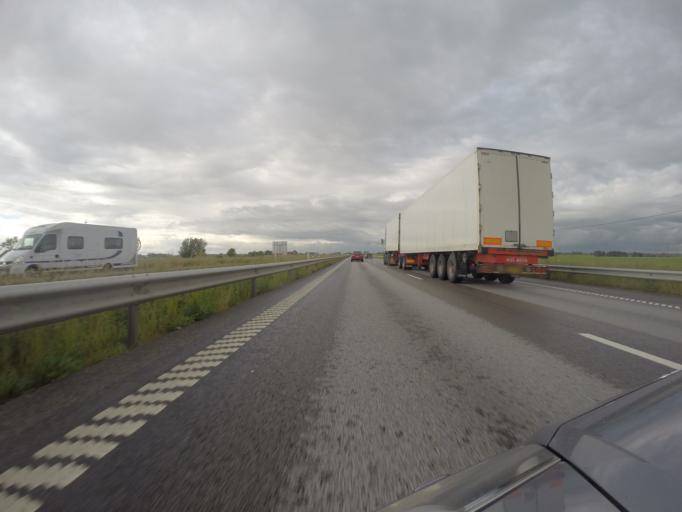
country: SE
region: Skane
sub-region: Lomma Kommun
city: Lomma
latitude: 55.6942
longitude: 13.0977
